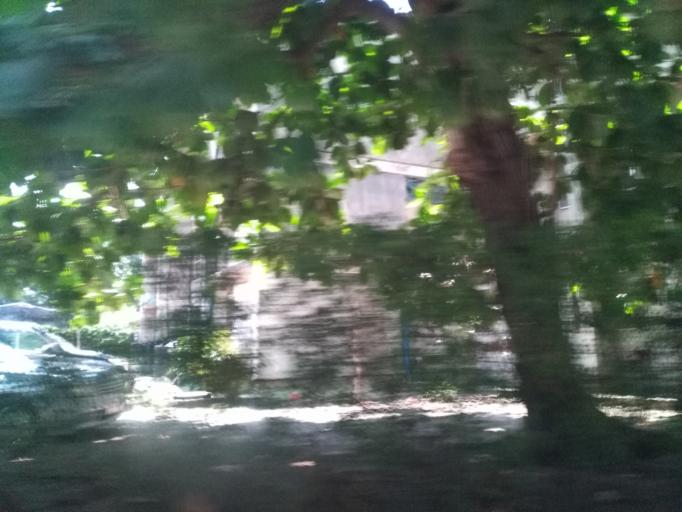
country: TZ
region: Dar es Salaam
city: Dar es Salaam
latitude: -6.8087
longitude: 39.2726
